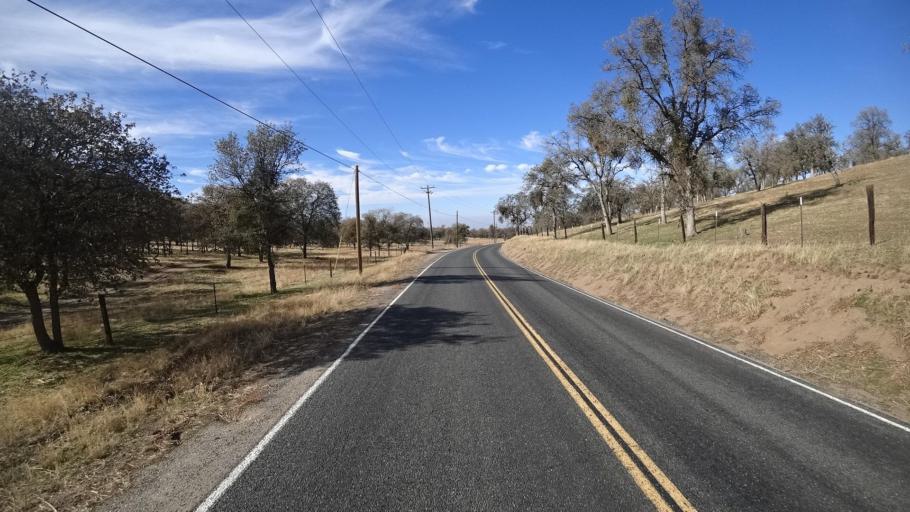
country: US
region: California
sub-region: Kern County
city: Alta Sierra
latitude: 35.6458
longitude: -118.7857
